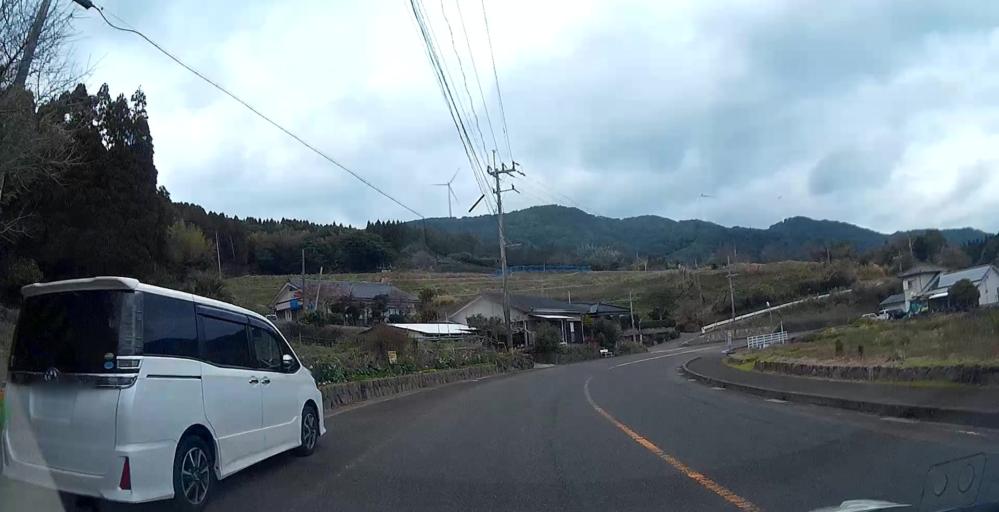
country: JP
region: Kagoshima
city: Akune
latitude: 32.1015
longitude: 130.1668
